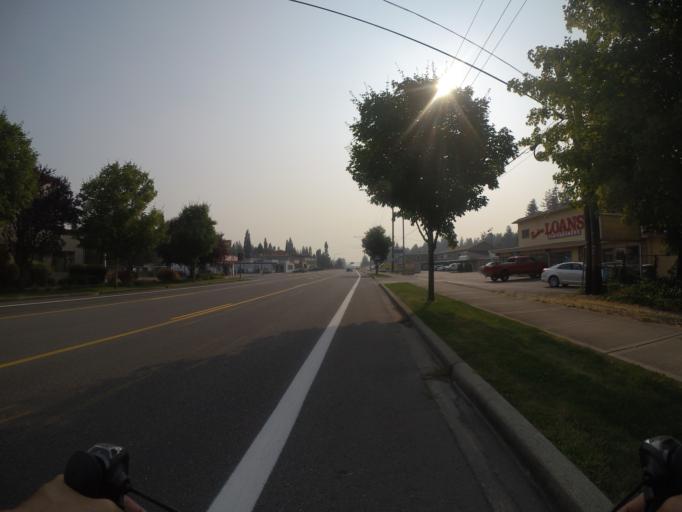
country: US
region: Washington
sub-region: Pierce County
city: McChord Air Force Base
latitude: 47.1412
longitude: -122.5183
